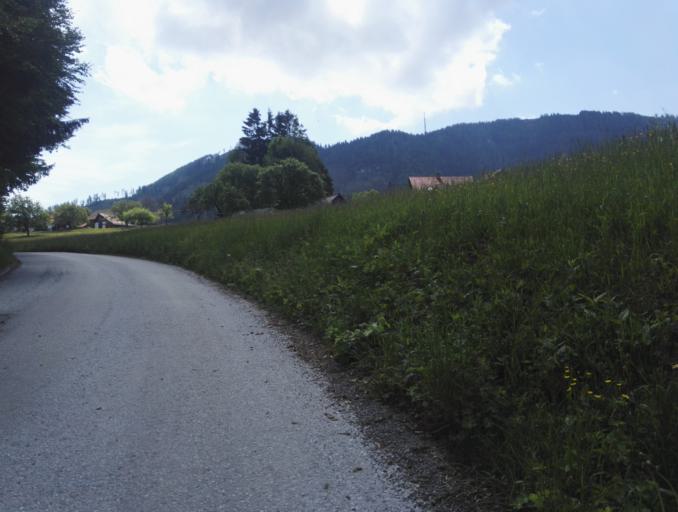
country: AT
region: Styria
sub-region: Politischer Bezirk Graz-Umgebung
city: Semriach
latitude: 47.2127
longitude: 15.4538
